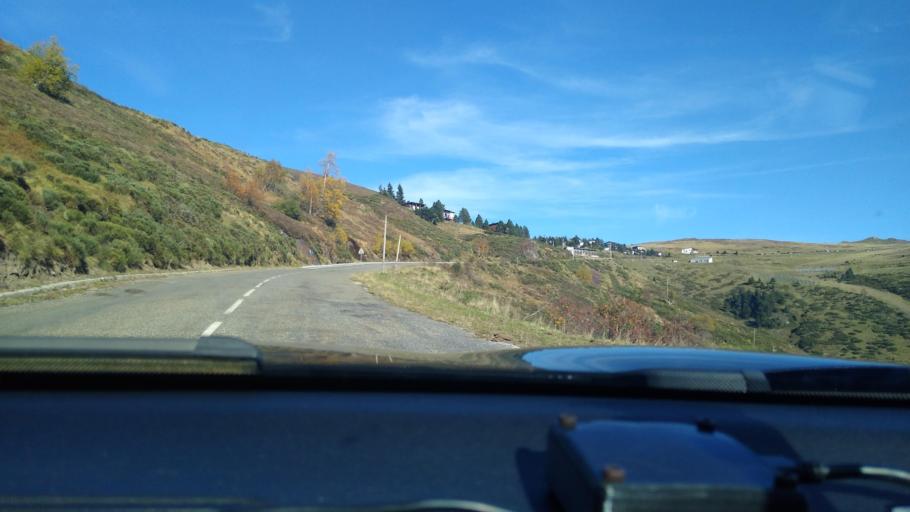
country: FR
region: Midi-Pyrenees
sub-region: Departement de l'Ariege
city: Ax-les-Thermes
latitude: 42.7323
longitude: 1.9774
